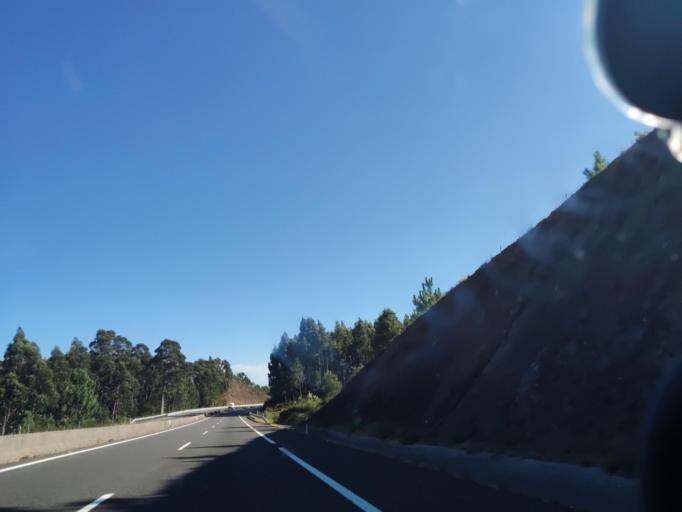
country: ES
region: Galicia
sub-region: Provincia da Coruna
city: Boiro
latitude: 42.5974
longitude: -8.9692
